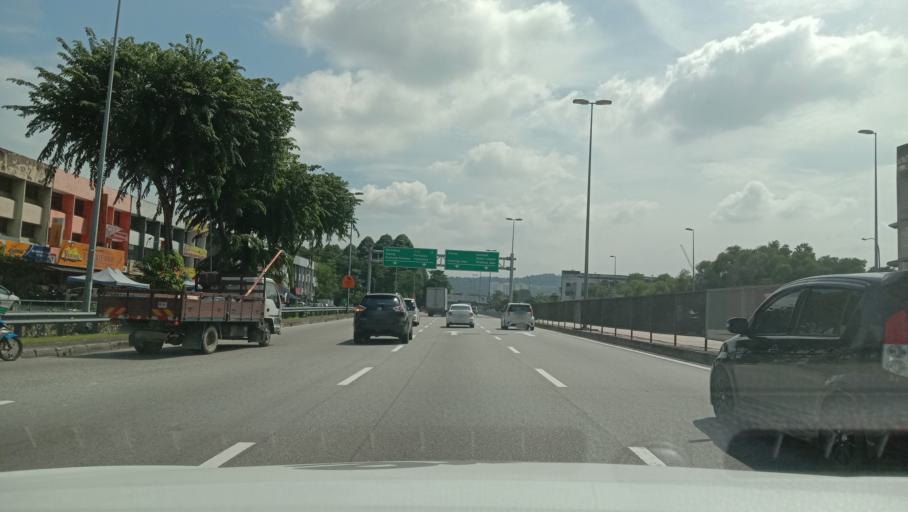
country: MY
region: Selangor
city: Subang Jaya
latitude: 3.0204
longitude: 101.6063
